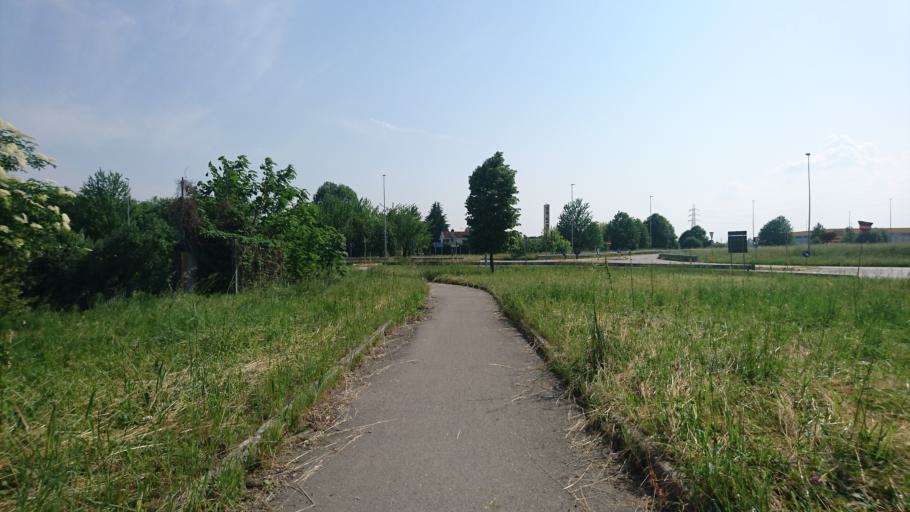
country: IT
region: Veneto
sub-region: Provincia di Padova
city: Ponte San Nicolo
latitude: 45.3820
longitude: 11.9407
